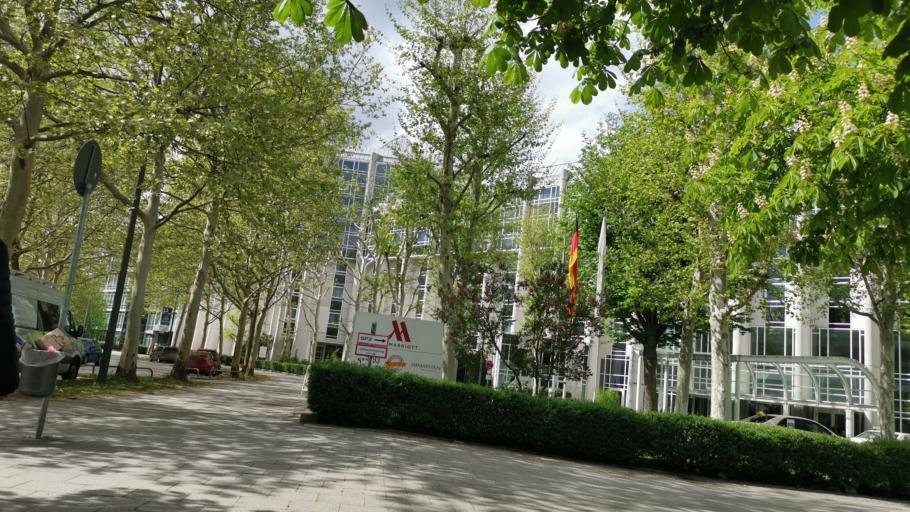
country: DE
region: Bavaria
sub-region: Upper Bavaria
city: Bogenhausen
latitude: 48.1741
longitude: 11.5930
